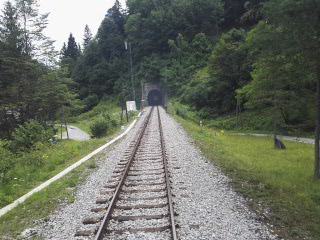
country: SI
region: Cerkno
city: Cerkno
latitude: 46.1743
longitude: 13.9151
